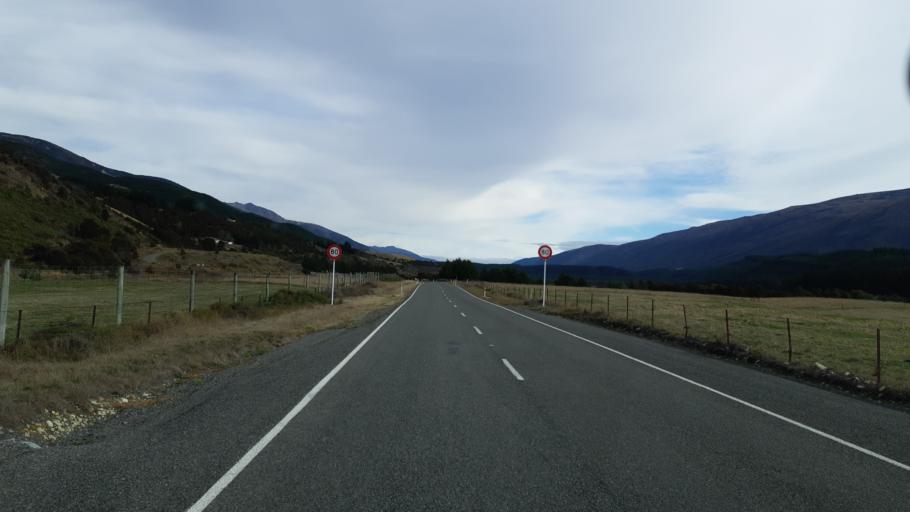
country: NZ
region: Tasman
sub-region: Tasman District
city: Wakefield
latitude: -41.6876
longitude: 173.1563
